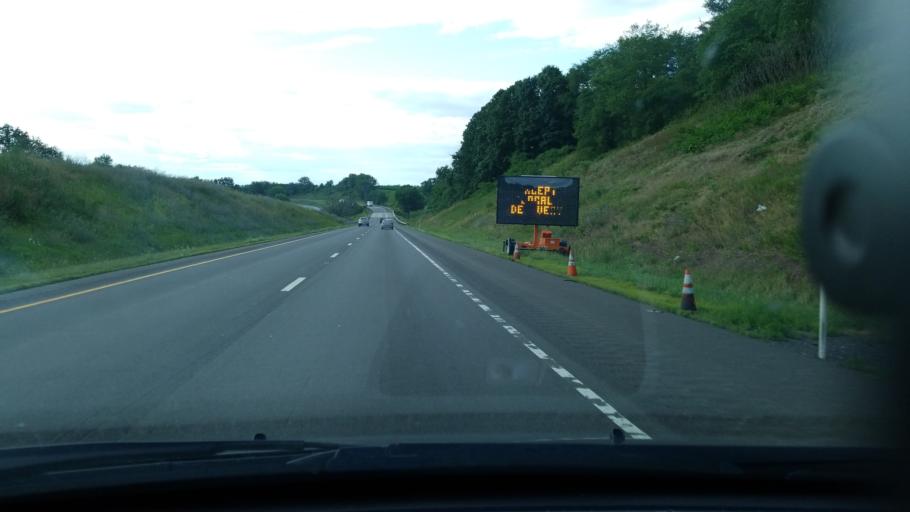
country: US
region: Pennsylvania
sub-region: Northumberland County
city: Milton
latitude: 41.0363
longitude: -76.8086
